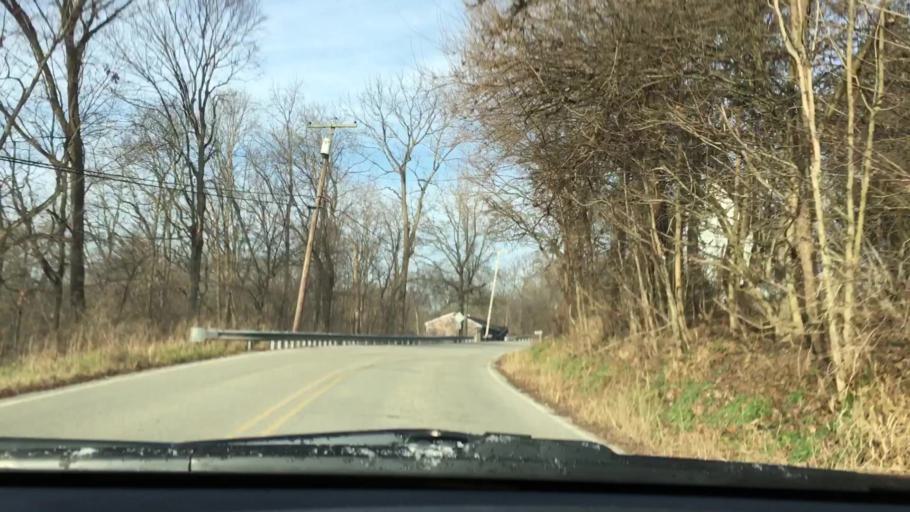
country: US
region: Pennsylvania
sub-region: Westmoreland County
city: Collinsburg
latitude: 40.2608
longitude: -79.7385
